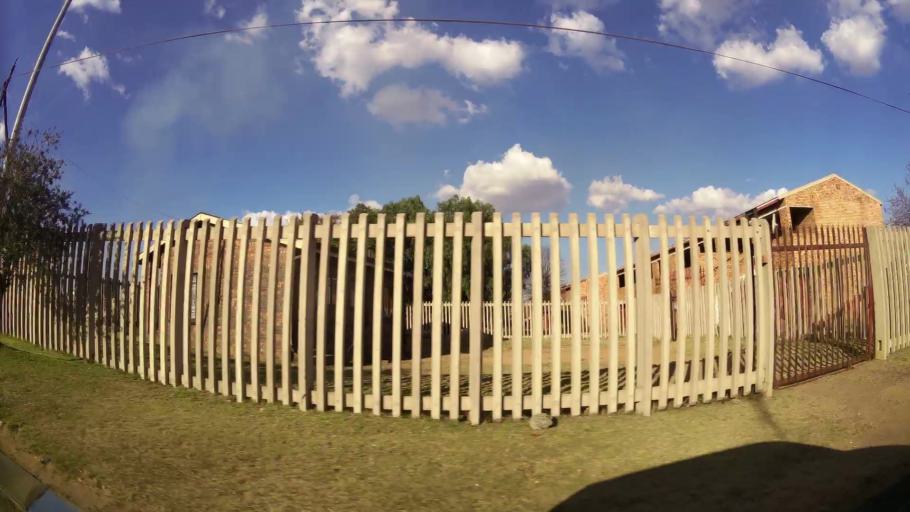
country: ZA
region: Mpumalanga
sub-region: Nkangala District Municipality
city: Witbank
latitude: -25.8670
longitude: 29.1738
